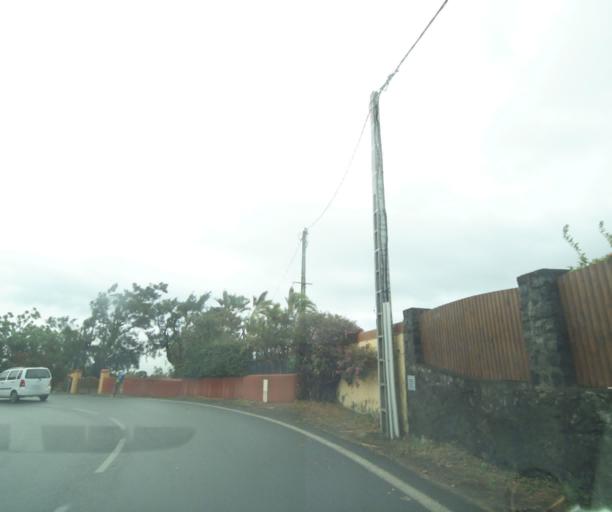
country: RE
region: Reunion
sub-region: Reunion
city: Saint-Paul
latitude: -21.0310
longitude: 55.2843
